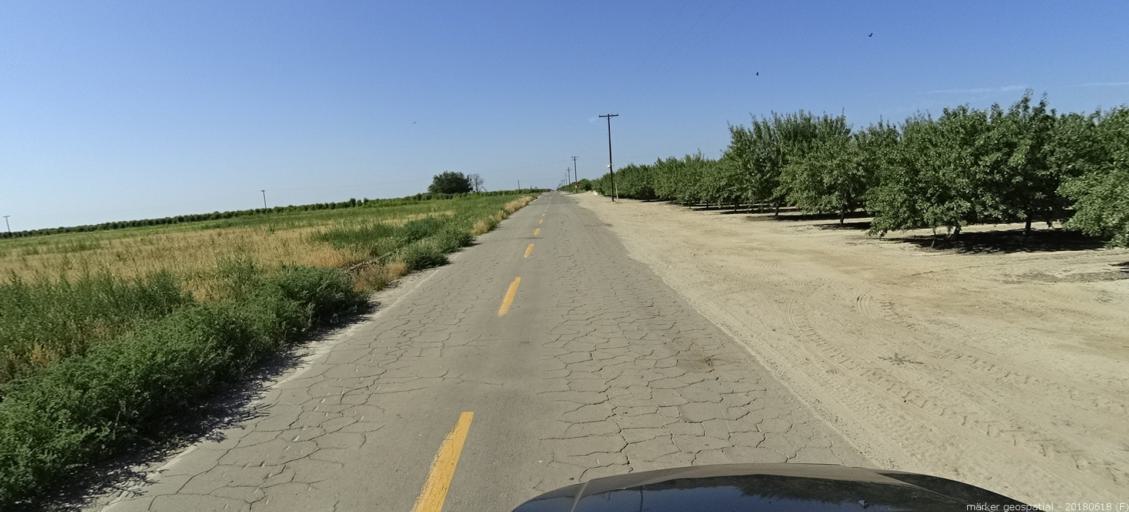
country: US
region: California
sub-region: Madera County
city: Parkwood
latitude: 36.8528
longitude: -120.1465
